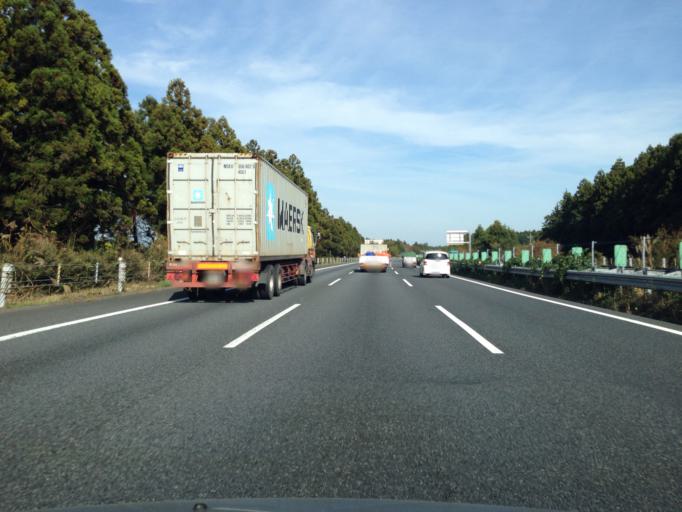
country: JP
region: Ibaraki
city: Tomobe
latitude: 36.2693
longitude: 140.3037
